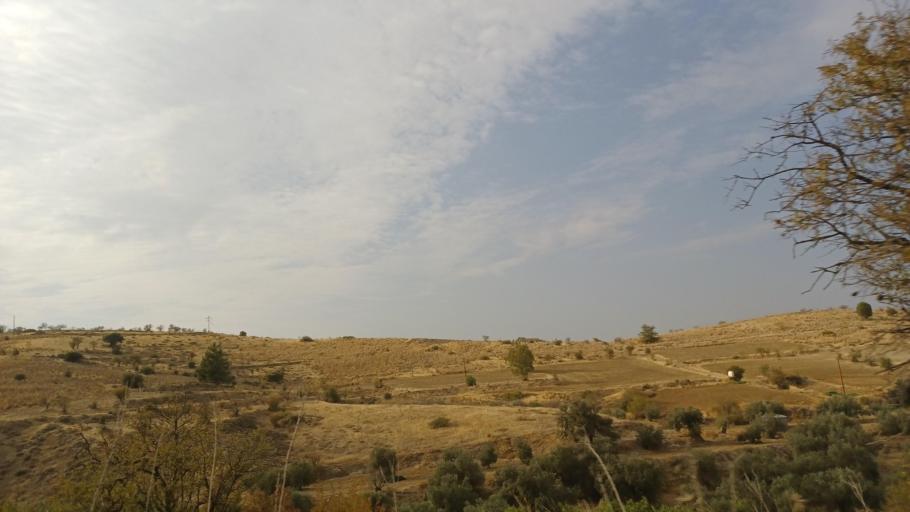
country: CY
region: Lefkosia
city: Peristerona
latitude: 35.0611
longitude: 33.0883
